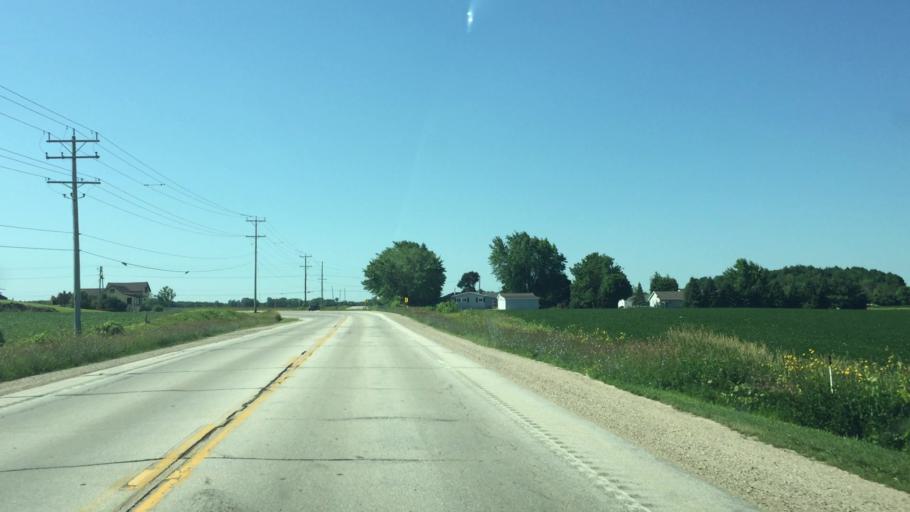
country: US
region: Wisconsin
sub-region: Calumet County
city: Sherwood
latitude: 44.1435
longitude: -88.2649
